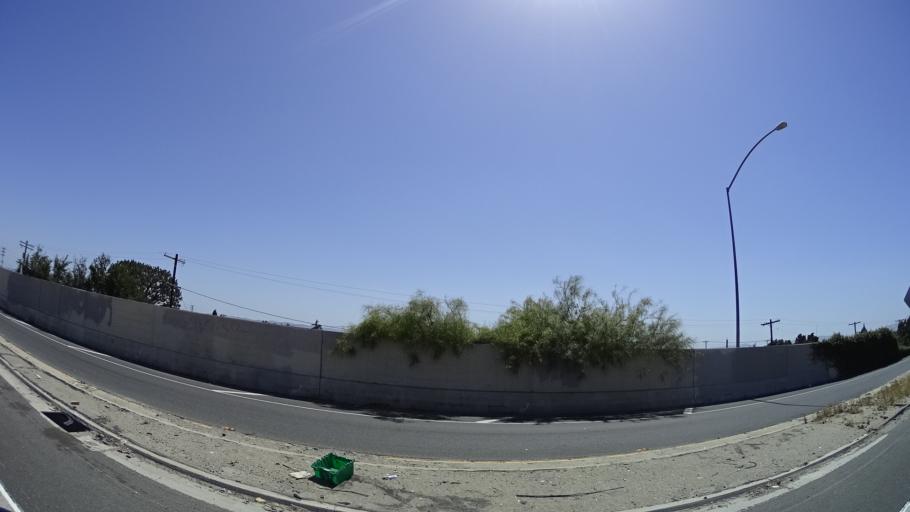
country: US
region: California
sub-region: Los Angeles County
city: San Fernando
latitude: 34.2549
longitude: -118.4335
